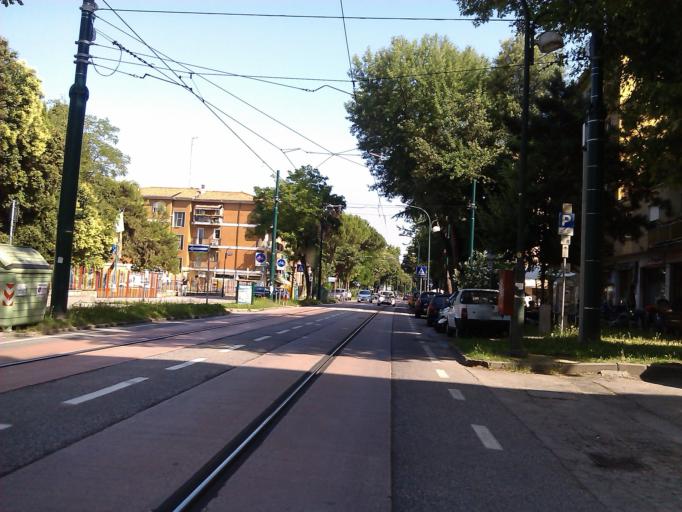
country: IT
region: Veneto
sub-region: Provincia di Venezia
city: Mestre
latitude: 45.4891
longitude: 12.2527
